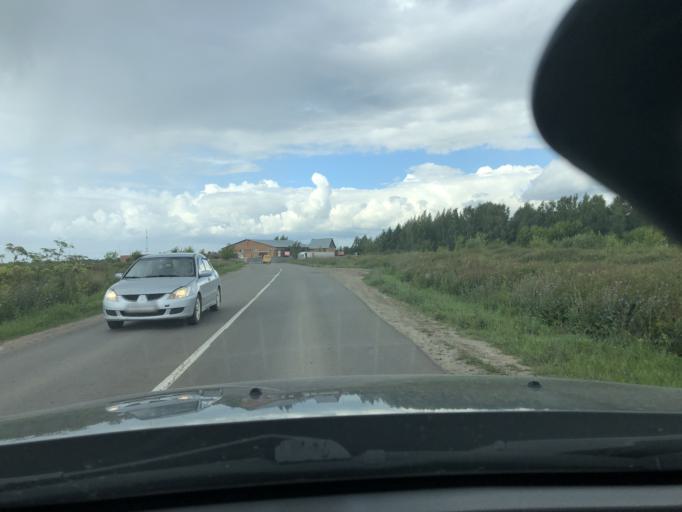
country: RU
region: Tula
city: Kamenetskiy
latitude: 54.0158
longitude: 38.2521
